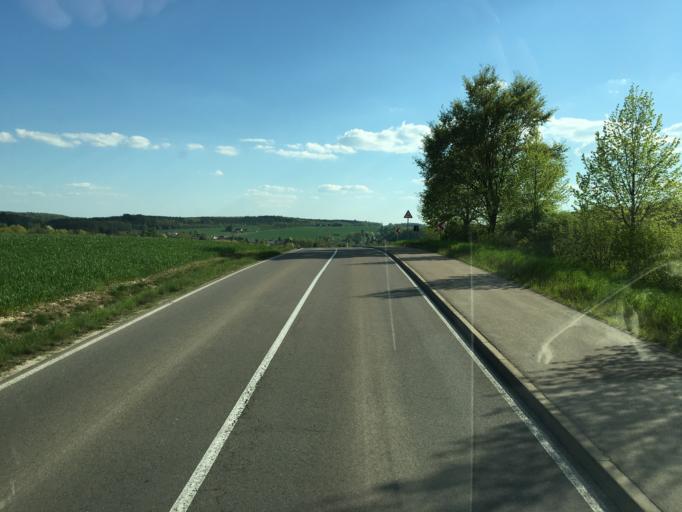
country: DE
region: Saxony
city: Rosswein
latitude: 51.0435
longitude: 13.1597
